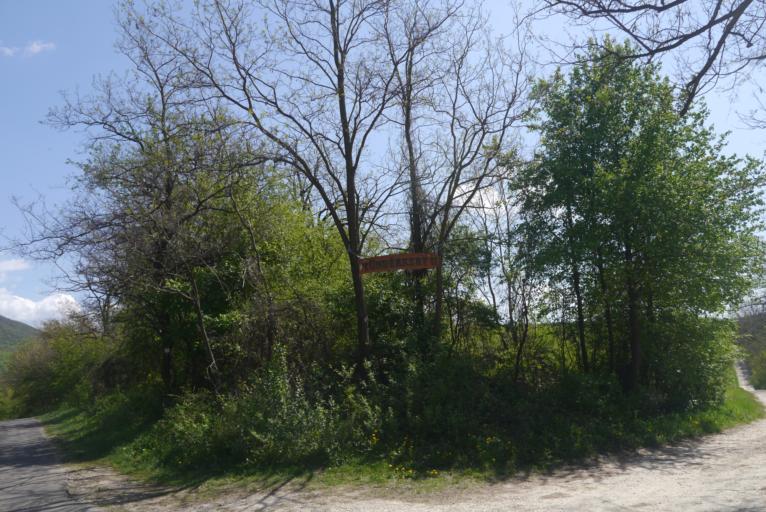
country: HU
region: Komarom-Esztergom
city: Kesztolc
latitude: 47.7106
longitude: 18.8189
